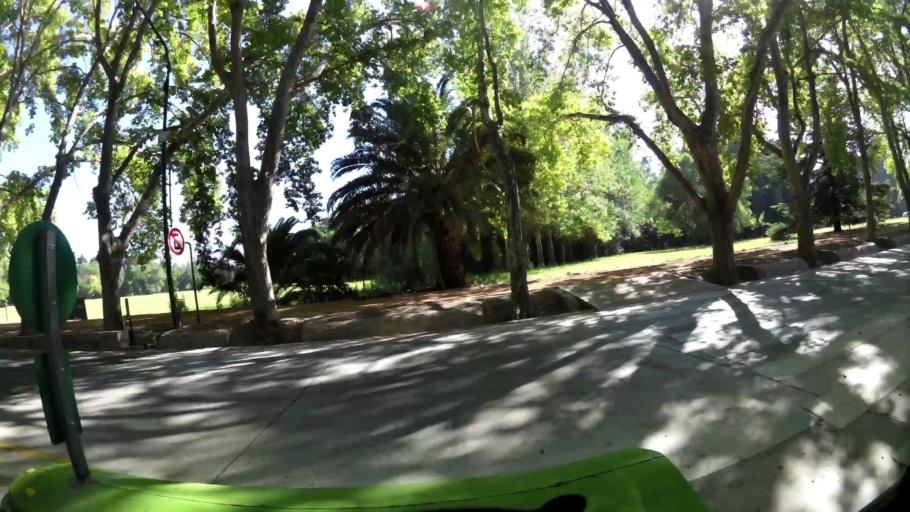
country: AR
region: Mendoza
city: Mendoza
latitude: -32.8885
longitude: -68.8680
